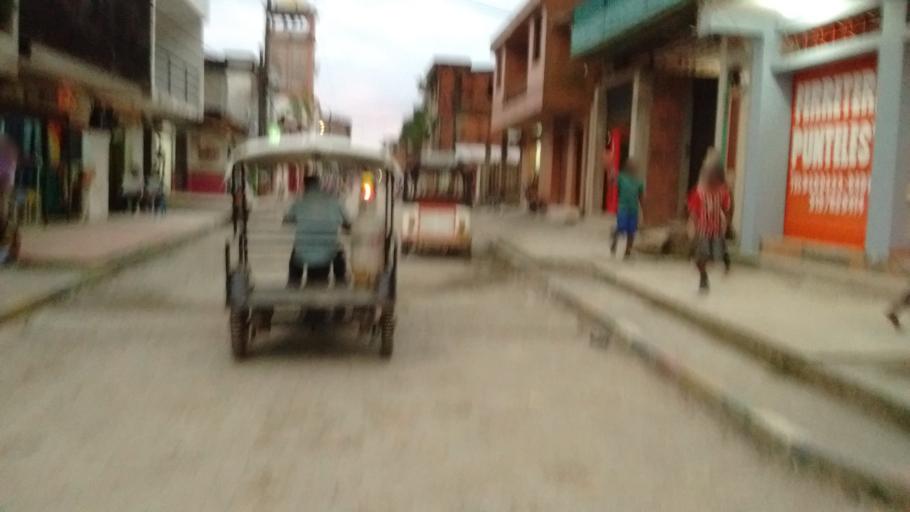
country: CO
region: Cauca
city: Guapi
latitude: 2.5698
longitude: -77.8821
